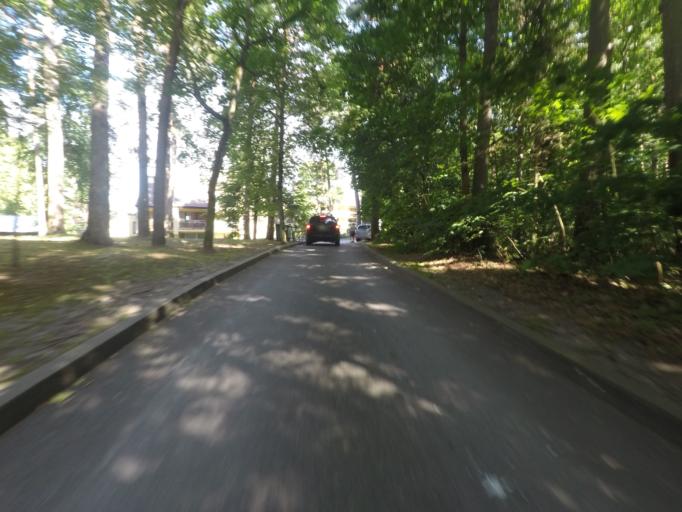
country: LT
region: Klaipedos apskritis
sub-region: Klaipeda
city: Klaipeda
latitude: 55.5433
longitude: 21.1175
